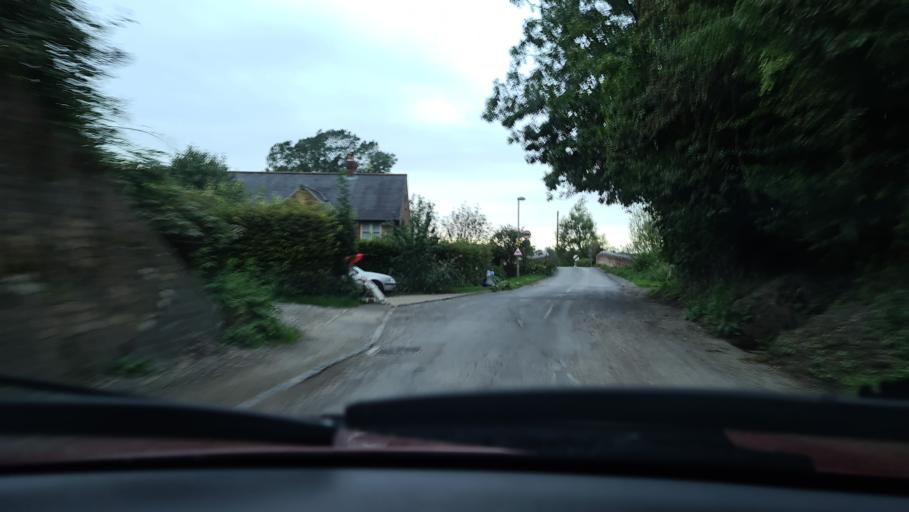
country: GB
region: England
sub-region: Oxfordshire
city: Somerton
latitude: 51.9568
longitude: -1.2786
